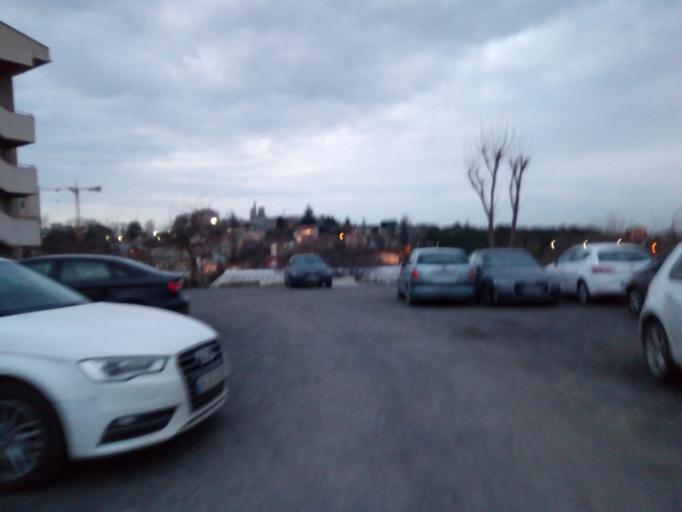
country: TR
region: Istanbul
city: Sisli
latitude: 41.1078
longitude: 29.0350
